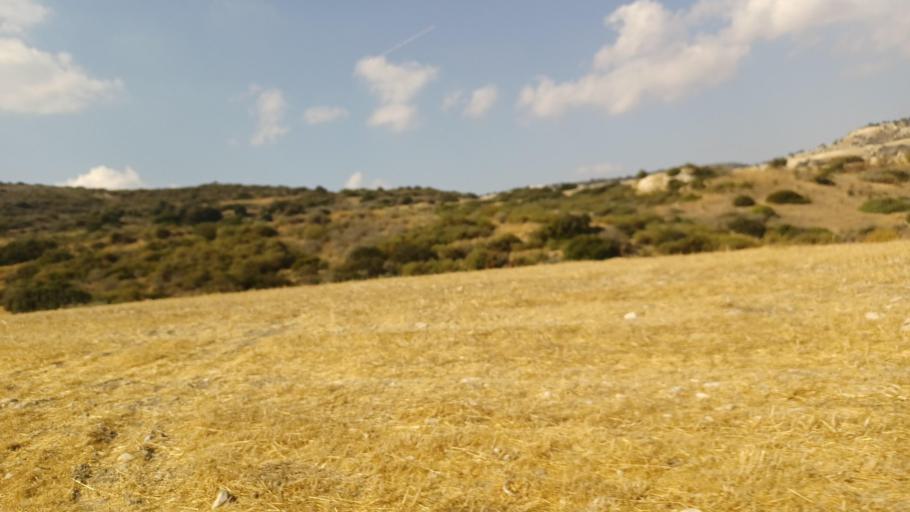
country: CY
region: Pafos
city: Polis
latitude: 34.9918
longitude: 32.4330
